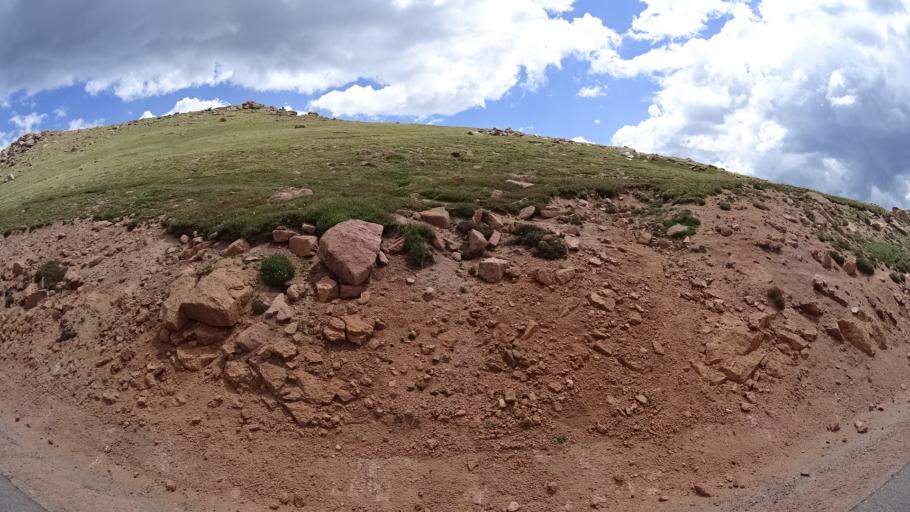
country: US
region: Colorado
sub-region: El Paso County
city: Cascade-Chipita Park
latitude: 38.8602
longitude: -105.0679
